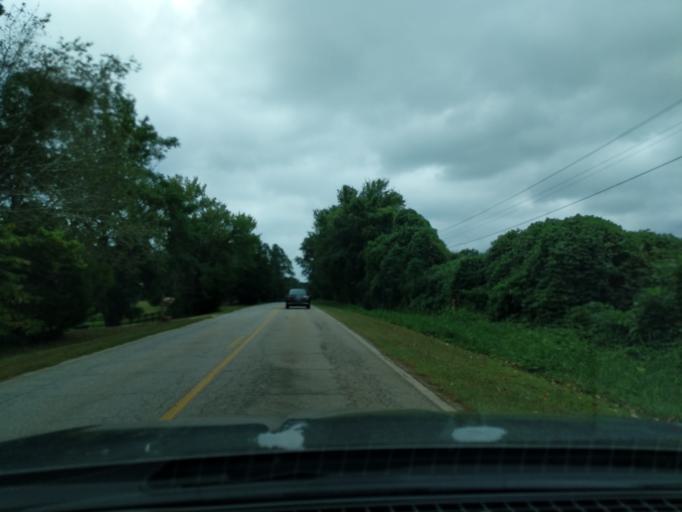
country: US
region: Georgia
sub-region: Columbia County
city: Appling
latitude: 33.6190
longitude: -82.4002
